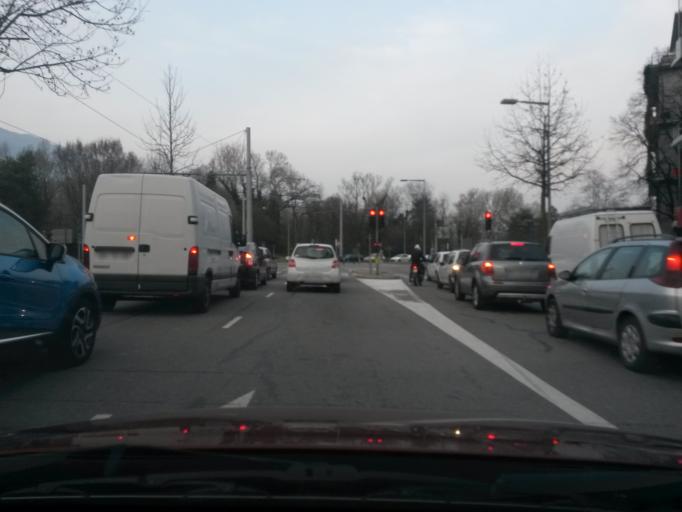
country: FR
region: Rhone-Alpes
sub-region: Departement de l'Isere
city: La Tronche
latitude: 45.1877
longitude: 5.7457
